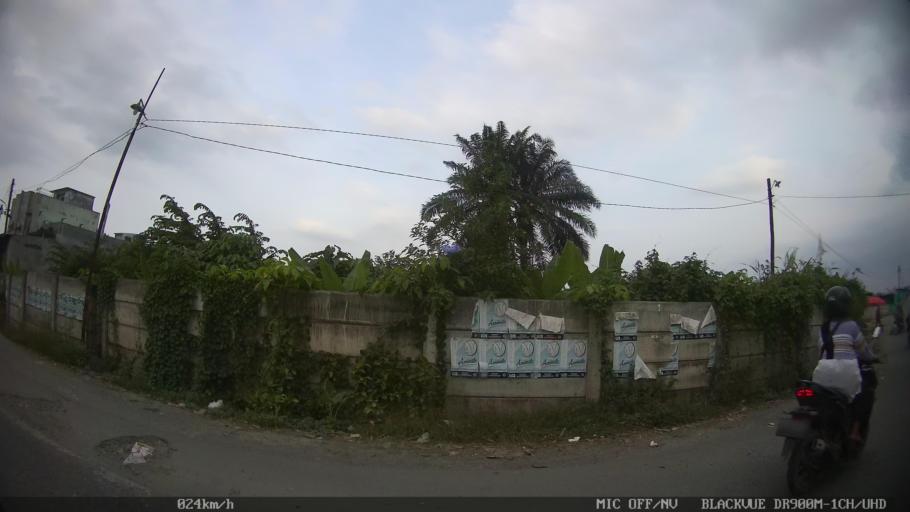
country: ID
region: North Sumatra
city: Sunggal
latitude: 3.5653
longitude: 98.6093
